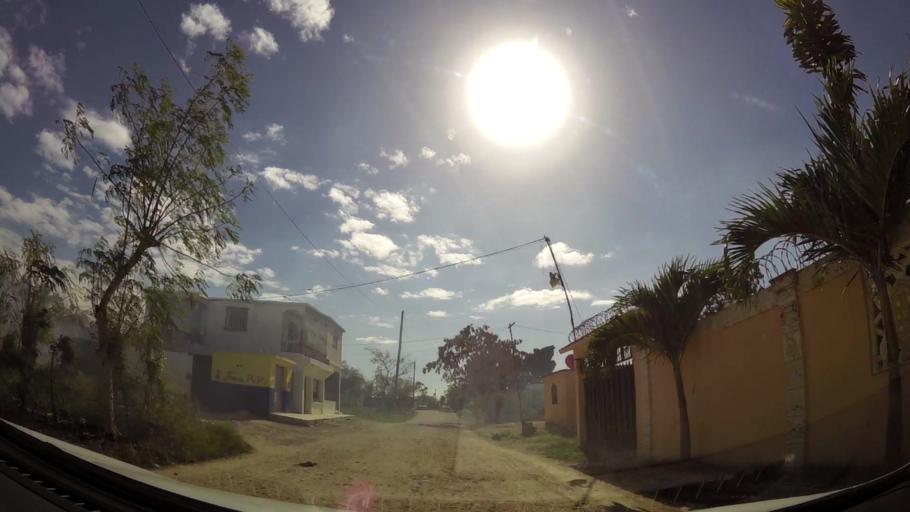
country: DO
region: Santo Domingo
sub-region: Santo Domingo
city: Boca Chica
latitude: 18.4644
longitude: -69.6041
